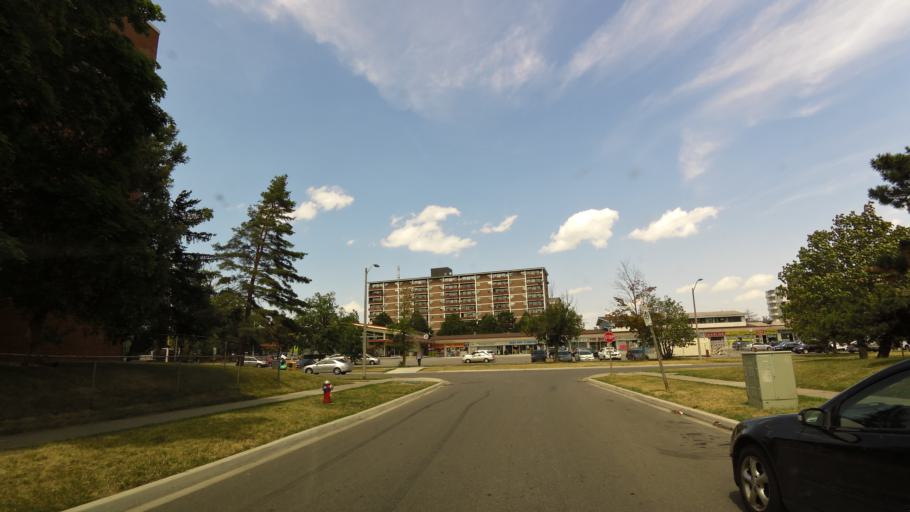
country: CA
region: Ontario
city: Etobicoke
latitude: 43.6236
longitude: -79.5896
